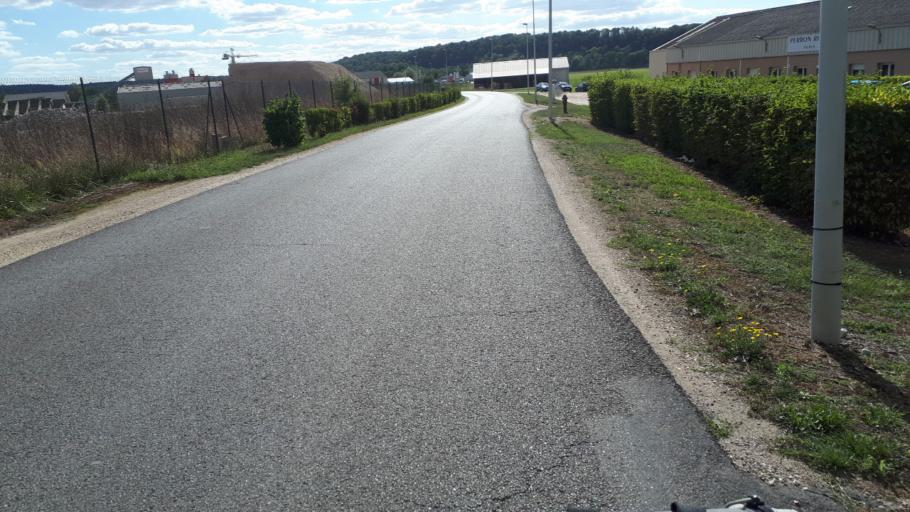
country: FR
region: Centre
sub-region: Departement du Loir-et-Cher
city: Villiers-sur-Loir
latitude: 47.7991
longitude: 0.9656
